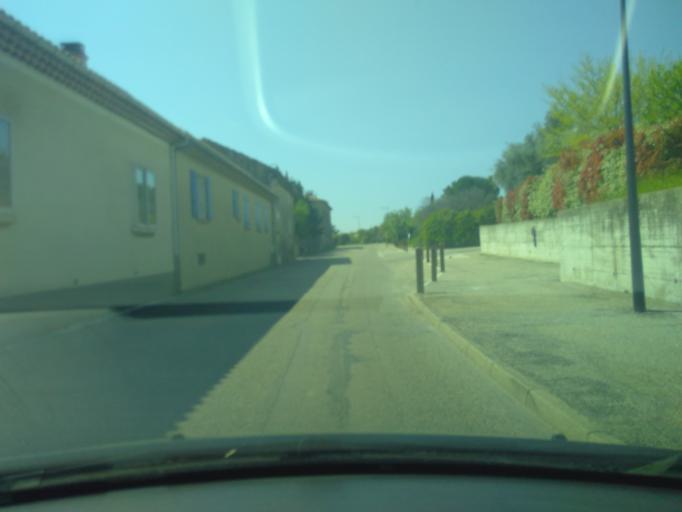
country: FR
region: Rhone-Alpes
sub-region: Departement de la Drome
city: Taulignan
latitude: 44.4436
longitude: 4.9755
